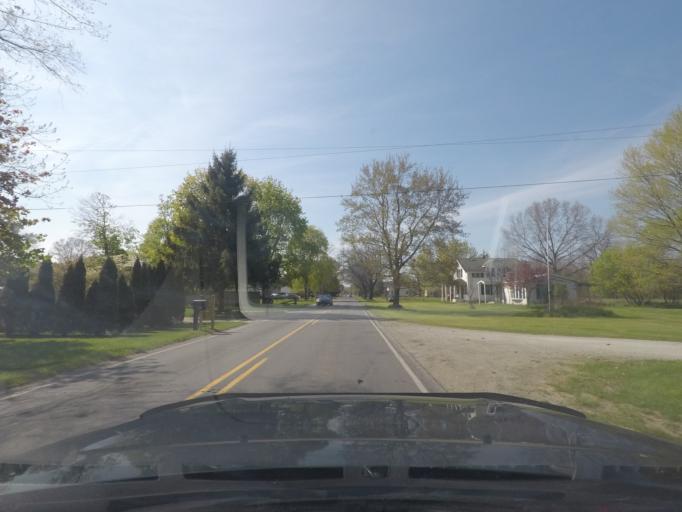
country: US
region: Indiana
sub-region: Saint Joseph County
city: Osceola
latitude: 41.7211
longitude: -86.0365
